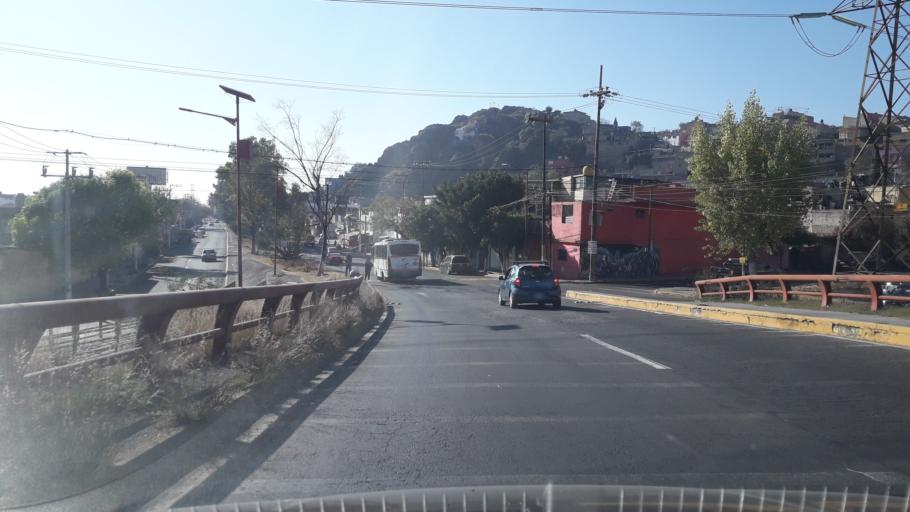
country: MX
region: Mexico
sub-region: Tlalnepantla de Baz
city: Puerto Escondido (Tepeolulco Puerto Escondido)
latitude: 19.5208
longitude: -99.0916
